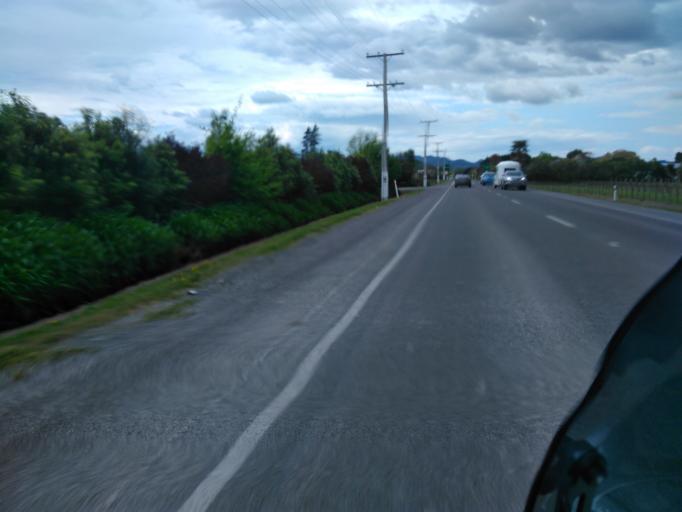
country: NZ
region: Gisborne
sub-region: Gisborne District
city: Gisborne
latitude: -38.6533
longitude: 177.9566
